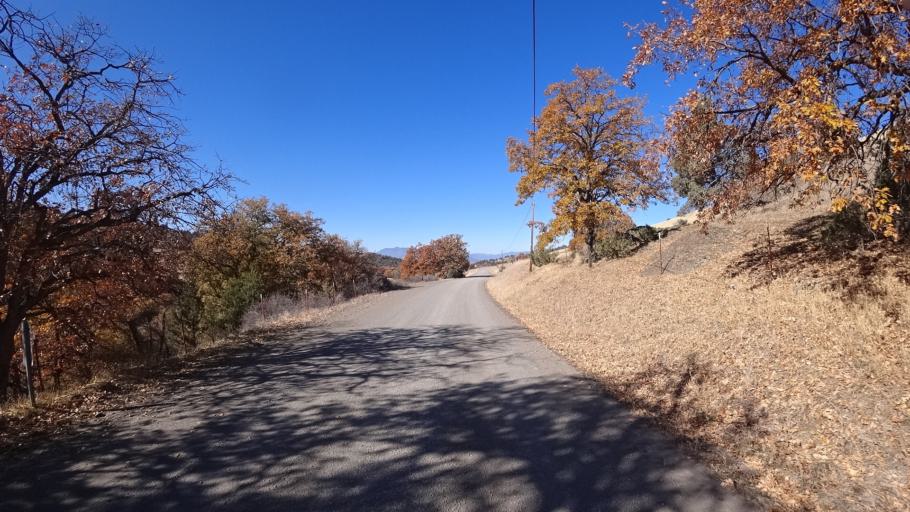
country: US
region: California
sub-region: Siskiyou County
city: Montague
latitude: 41.7941
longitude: -122.3625
